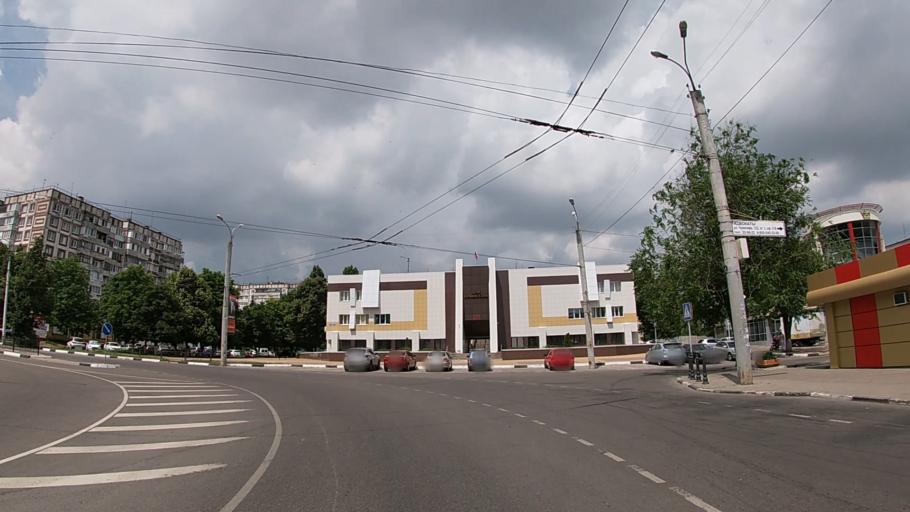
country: RU
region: Belgorod
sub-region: Belgorodskiy Rayon
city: Belgorod
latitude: 50.6129
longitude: 36.5908
